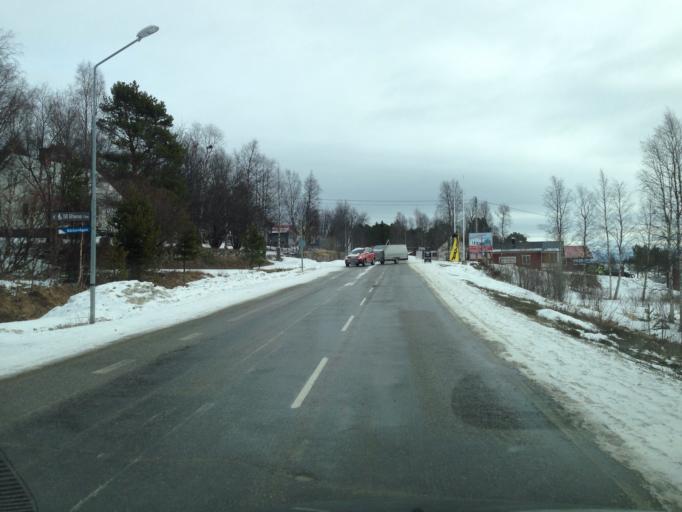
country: SE
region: Jaemtland
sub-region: Harjedalens Kommun
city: Sveg
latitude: 62.1121
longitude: 13.2760
